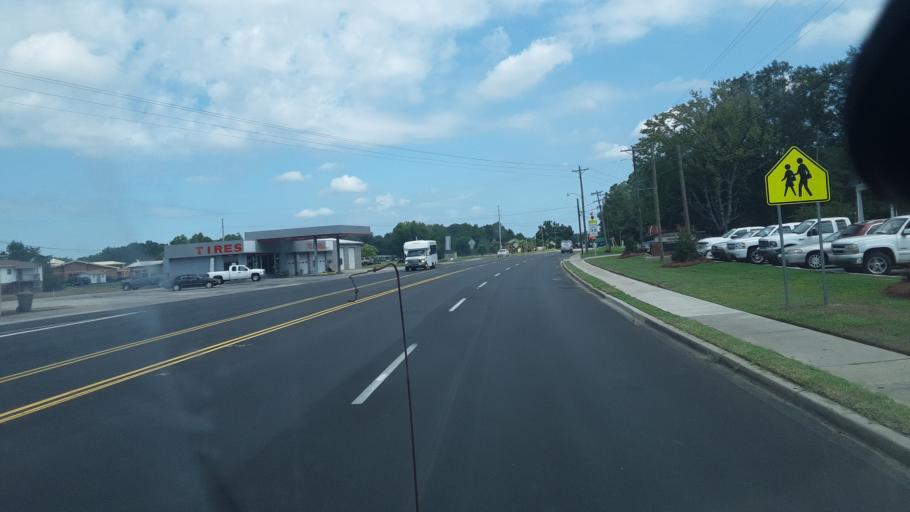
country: US
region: South Carolina
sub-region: Bamberg County
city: Bamberg
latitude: 33.3096
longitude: -81.0344
